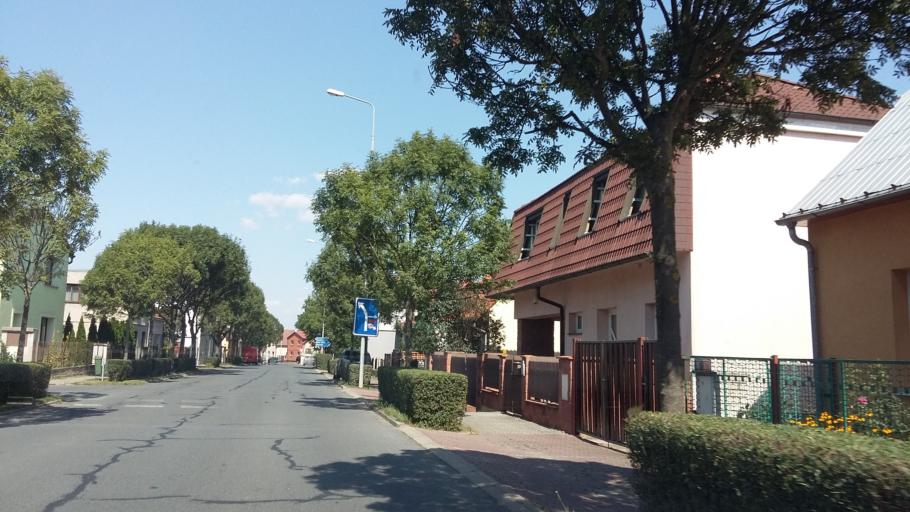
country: CZ
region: Central Bohemia
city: Zelenec
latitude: 50.1312
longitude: 14.6597
